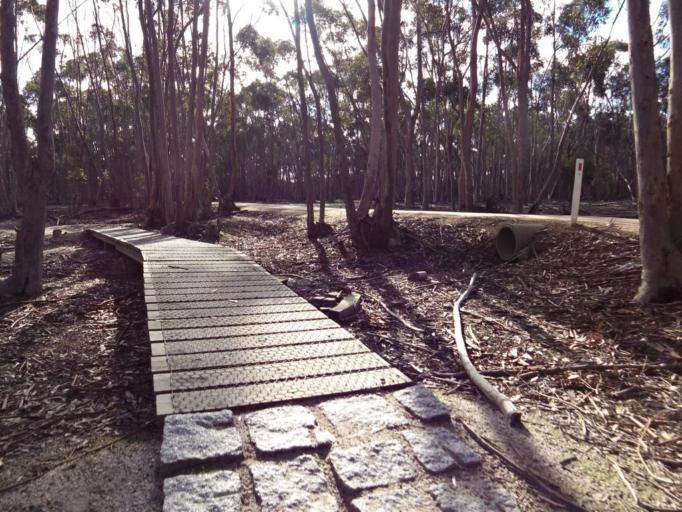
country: AU
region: Victoria
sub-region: Greater Geelong
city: Lara
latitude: -37.9412
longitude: 144.4115
